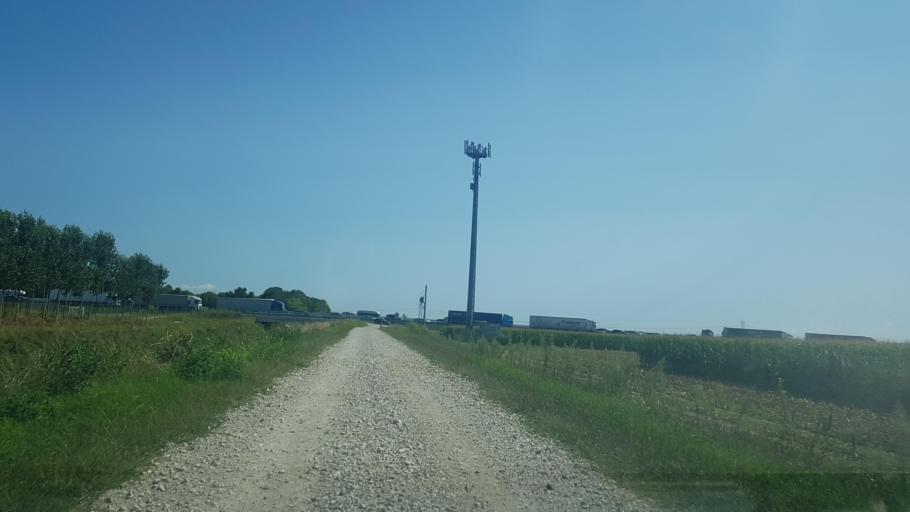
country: IT
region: Friuli Venezia Giulia
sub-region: Provincia di Udine
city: Muzzana del Turgnano
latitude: 45.8436
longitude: 13.1380
